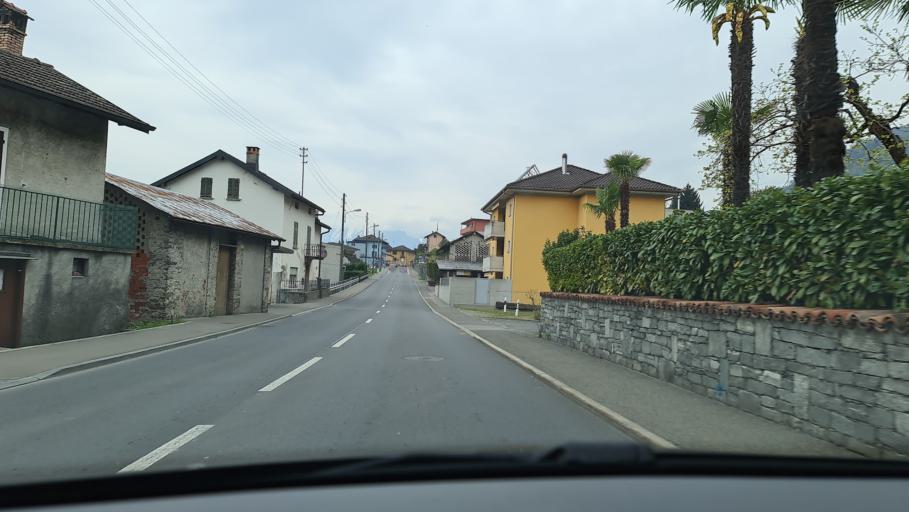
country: CH
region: Ticino
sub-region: Locarno District
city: Cugnasco
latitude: 46.1757
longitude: 8.9221
